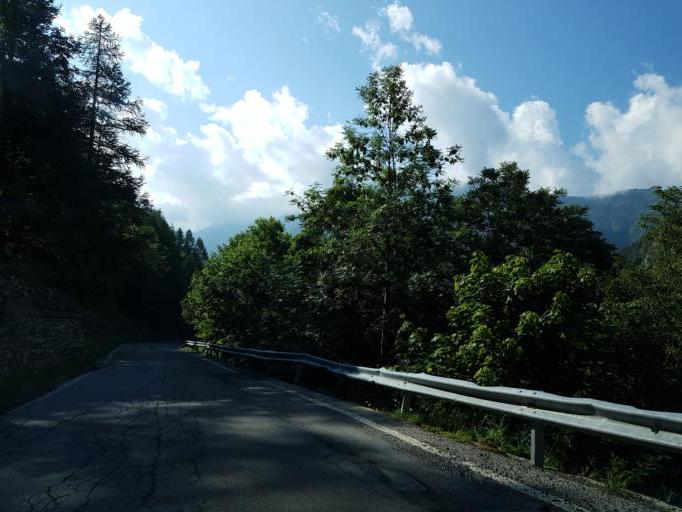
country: IT
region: Piedmont
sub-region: Provincia di Cuneo
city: Casteldelfino
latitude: 44.6030
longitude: 7.0641
